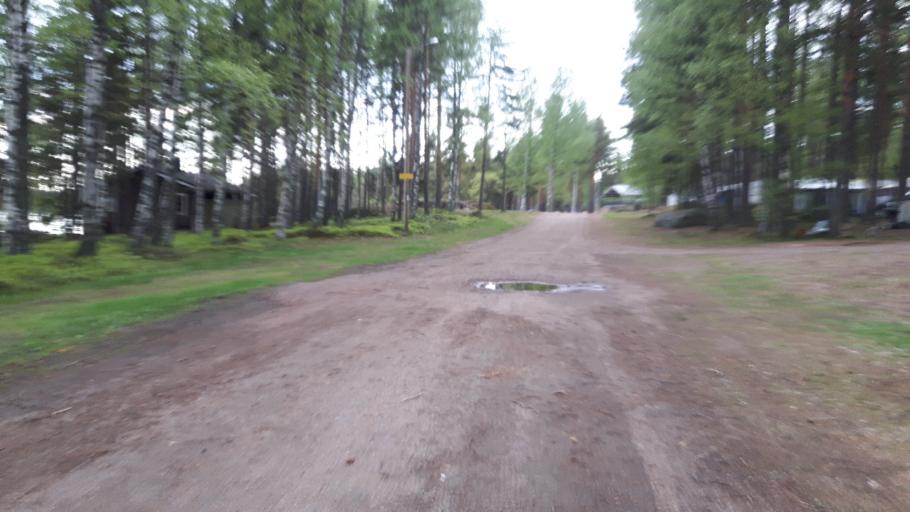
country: FI
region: Kymenlaakso
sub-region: Kotka-Hamina
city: Hamina
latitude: 60.5252
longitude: 27.2552
